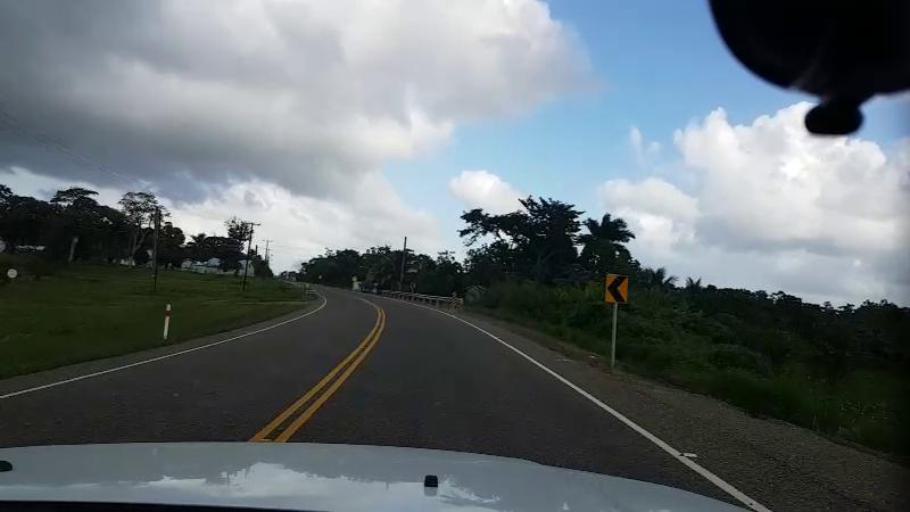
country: BZ
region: Stann Creek
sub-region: Dangriga
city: Dangriga
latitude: 16.9919
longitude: -88.3777
